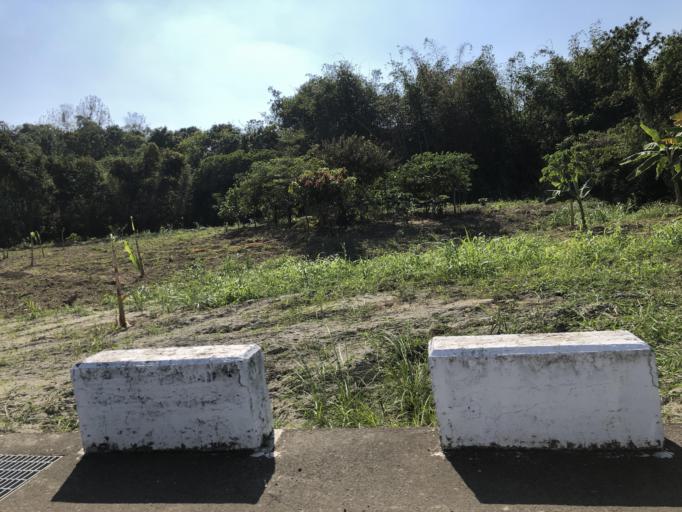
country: TW
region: Taiwan
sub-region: Tainan
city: Tainan
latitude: 23.0349
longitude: 120.3497
